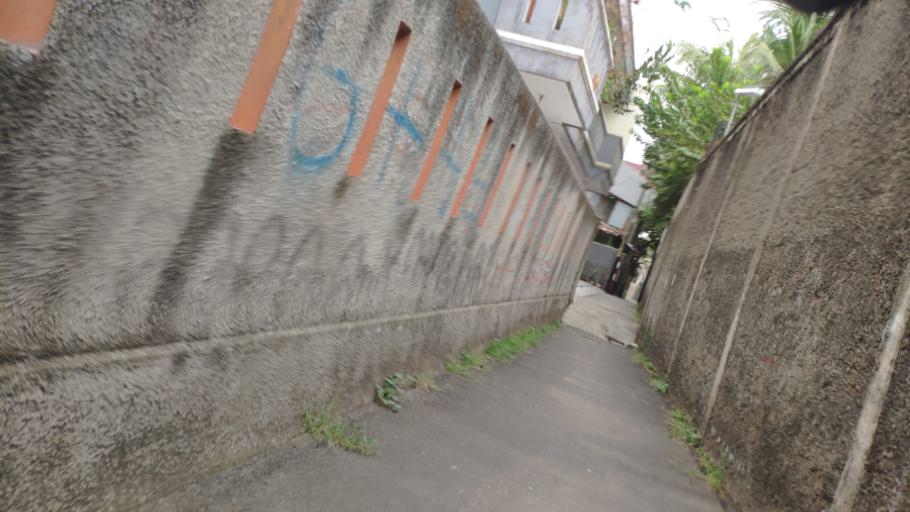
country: ID
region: Jakarta Raya
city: Jakarta
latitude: -6.2653
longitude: 106.7948
